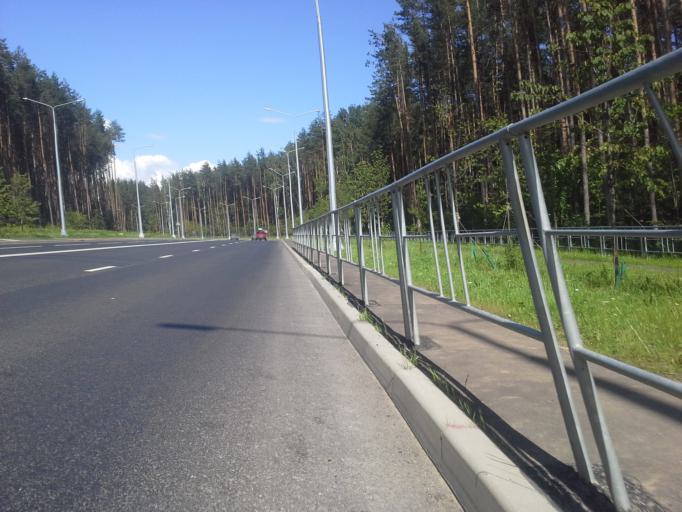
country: RU
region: Moskovskaya
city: Kokoshkino
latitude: 55.5696
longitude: 37.1585
